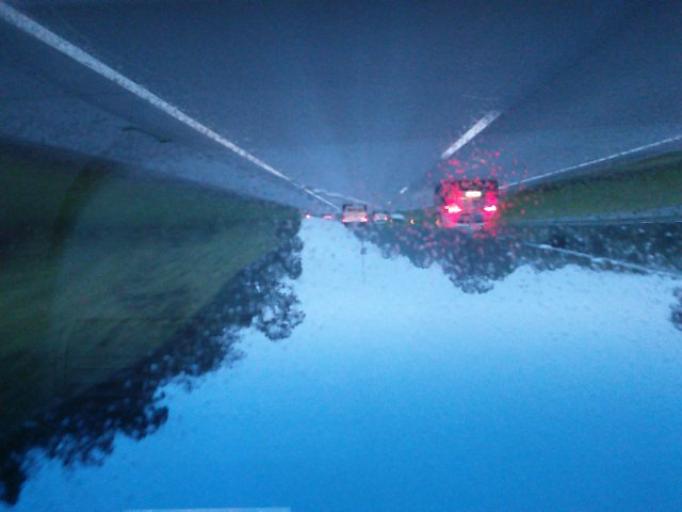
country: BR
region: Sao Paulo
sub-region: Juquitiba
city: Juquitiba
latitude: -23.9605
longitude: -47.1194
